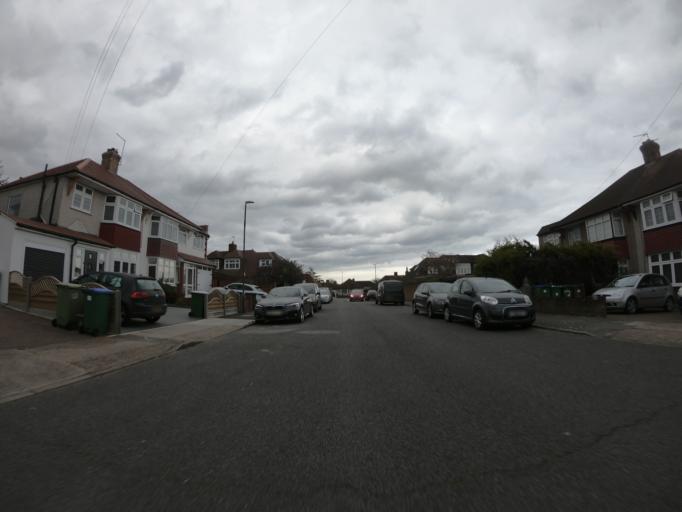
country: GB
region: England
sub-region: Greater London
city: Bexleyheath
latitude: 51.4777
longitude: 0.1377
